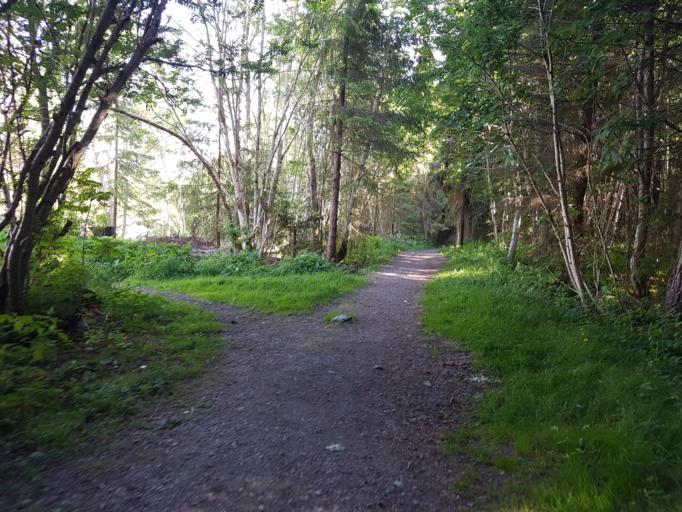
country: NO
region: Sor-Trondelag
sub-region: Trondheim
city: Trondheim
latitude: 63.3983
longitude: 10.3232
